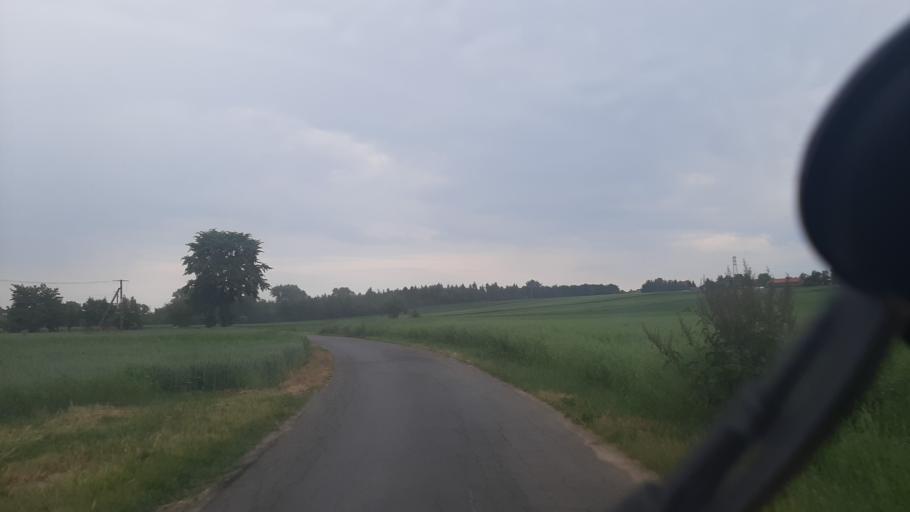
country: PL
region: Lublin Voivodeship
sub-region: Powiat lubelski
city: Garbow
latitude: 51.3513
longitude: 22.3588
